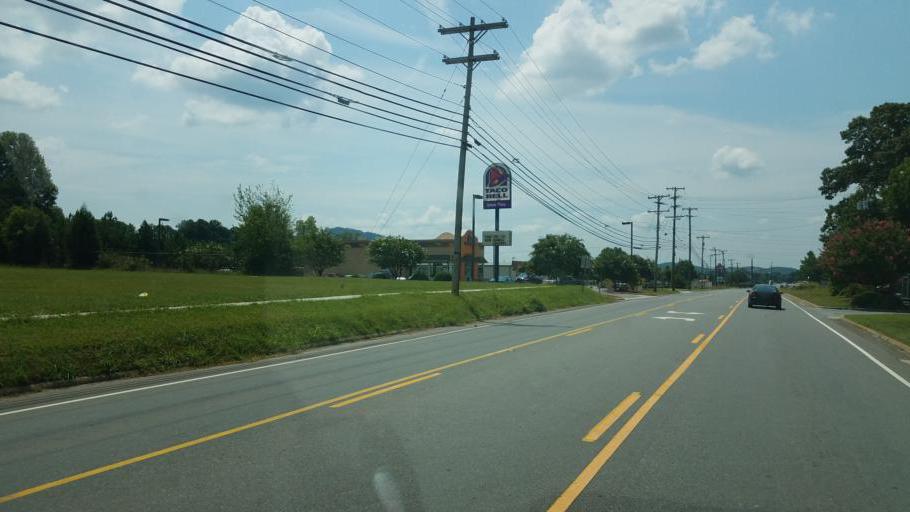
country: US
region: North Carolina
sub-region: Cleveland County
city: Kings Mountain
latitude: 35.2322
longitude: -81.3332
